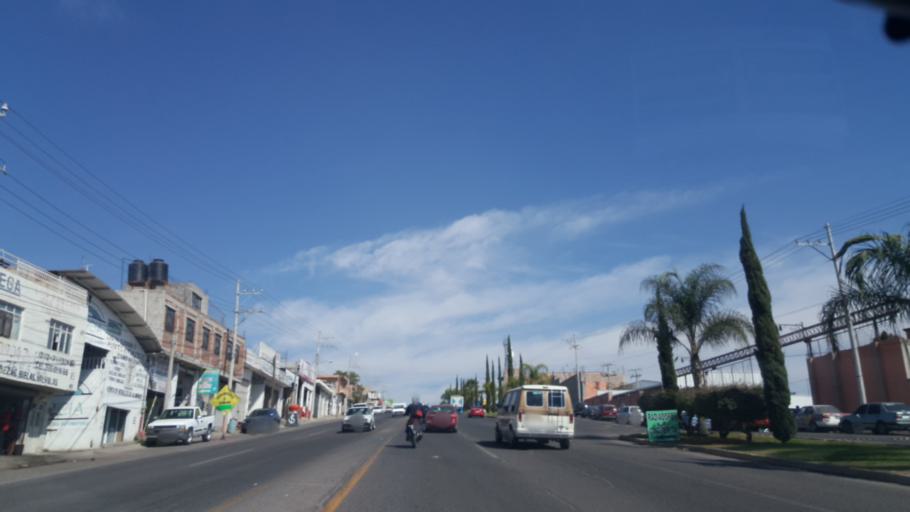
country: MX
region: Jalisco
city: San Juan de los Lagos
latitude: 21.2563
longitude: -102.3248
